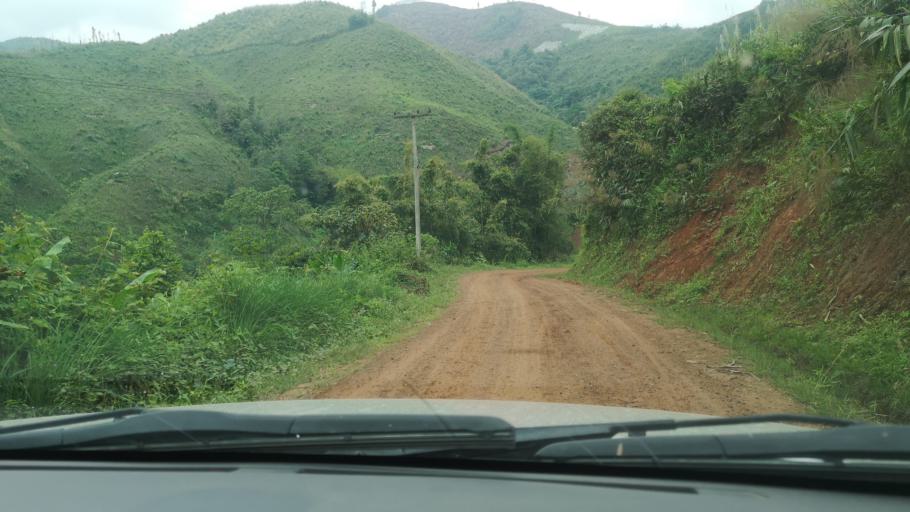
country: LA
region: Oudomxai
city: Muang La
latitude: 21.1671
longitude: 101.8894
